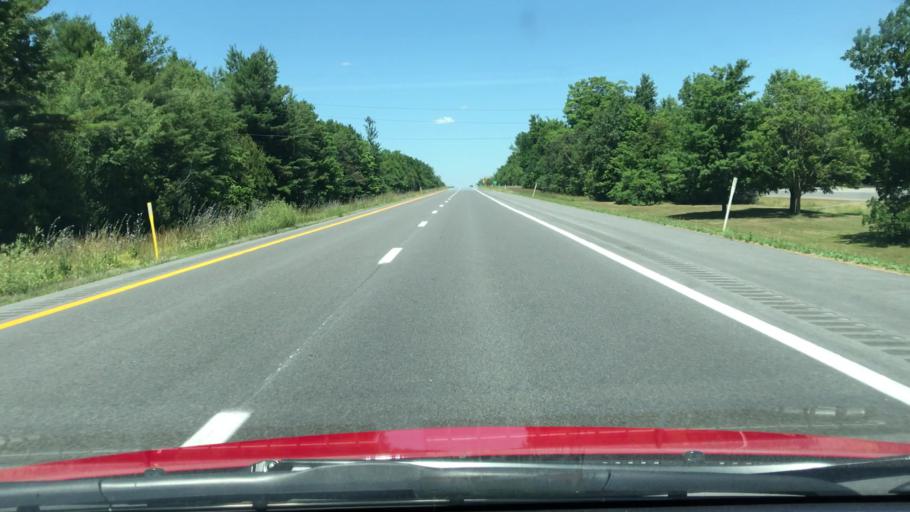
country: US
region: New York
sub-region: Clinton County
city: Cumberland Head
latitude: 44.8047
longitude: -73.4438
